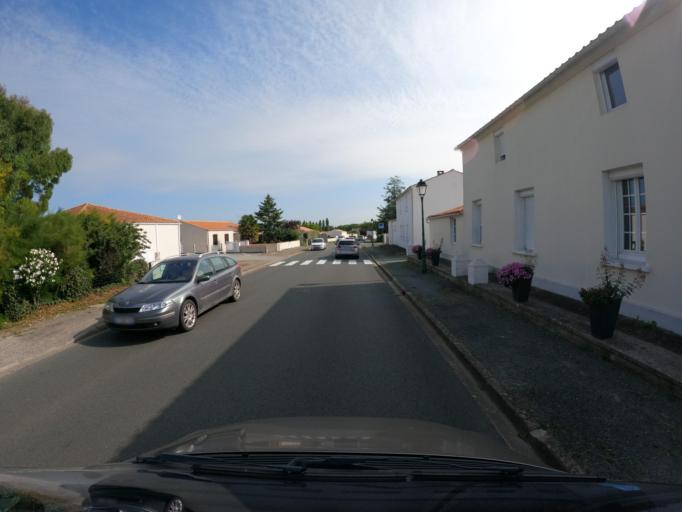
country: FR
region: Pays de la Loire
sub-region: Departement de la Vendee
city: Triaize
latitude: 46.3569
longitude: -1.2452
